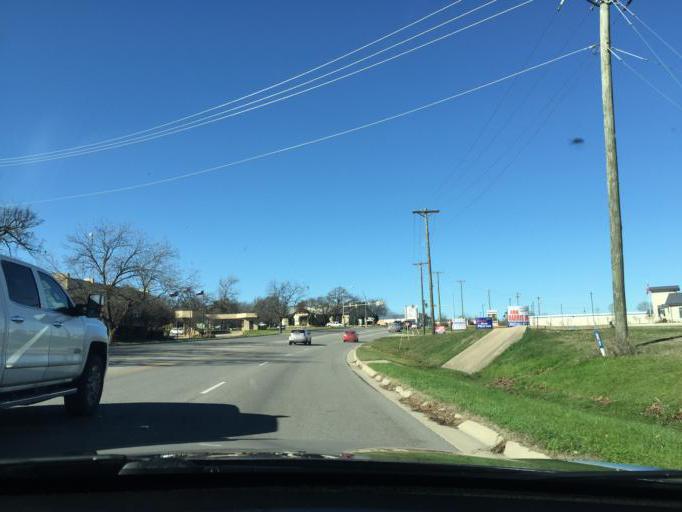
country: US
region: Texas
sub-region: Parker County
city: Weatherford
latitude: 32.7410
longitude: -97.7814
